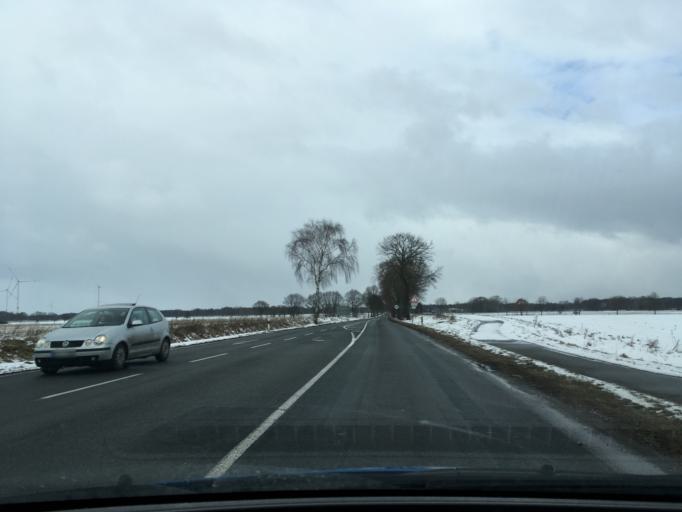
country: DE
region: Lower Saxony
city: Wulfsen
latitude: 53.3117
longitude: 10.1671
